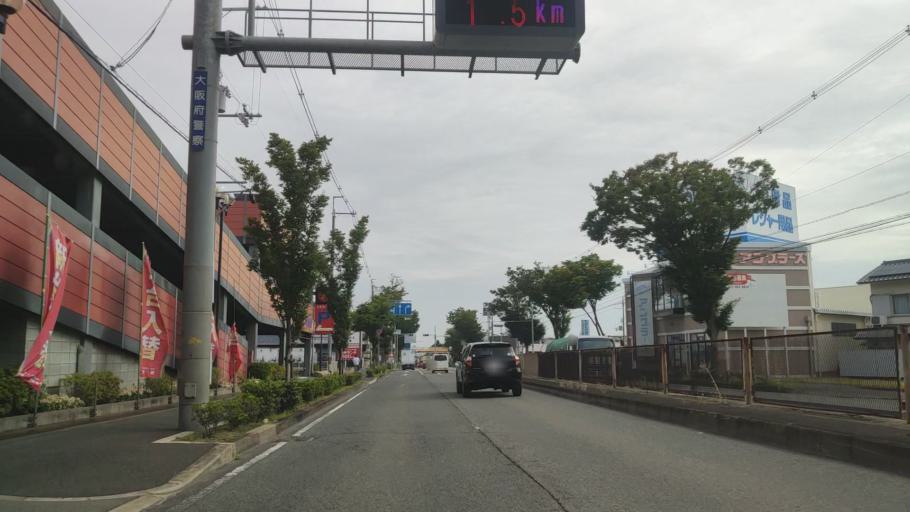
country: JP
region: Osaka
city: Tondabayashicho
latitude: 34.4524
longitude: 135.5604
